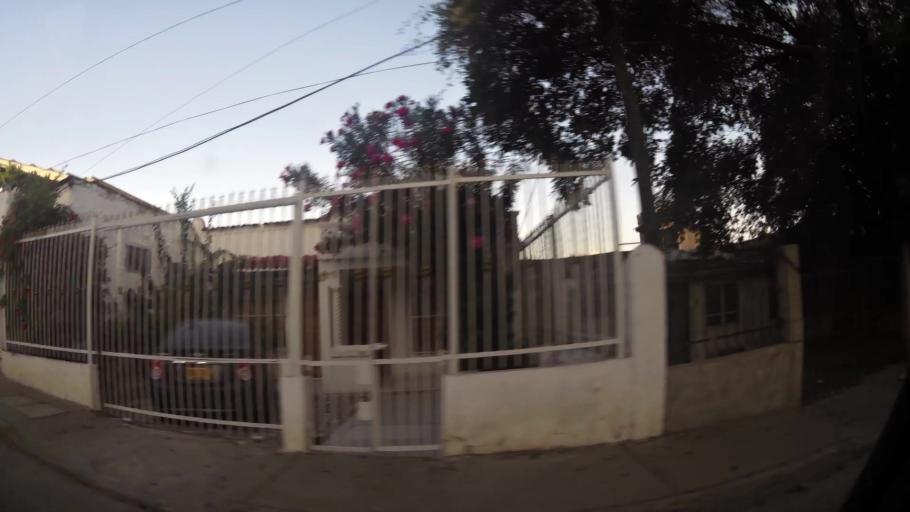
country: CO
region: Bolivar
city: Cartagena
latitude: 10.4265
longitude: -75.5371
